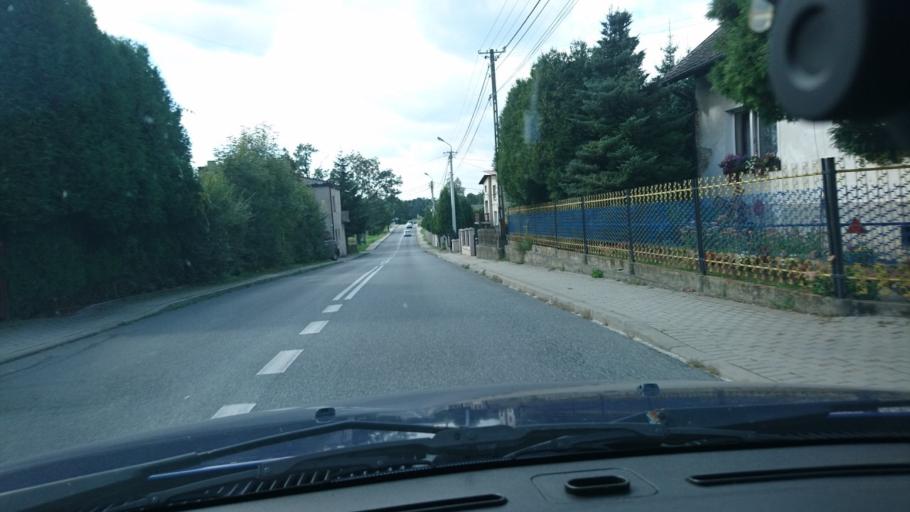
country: PL
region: Silesian Voivodeship
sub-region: Powiat bielski
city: Czechowice-Dziedzice
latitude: 49.9018
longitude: 18.9865
